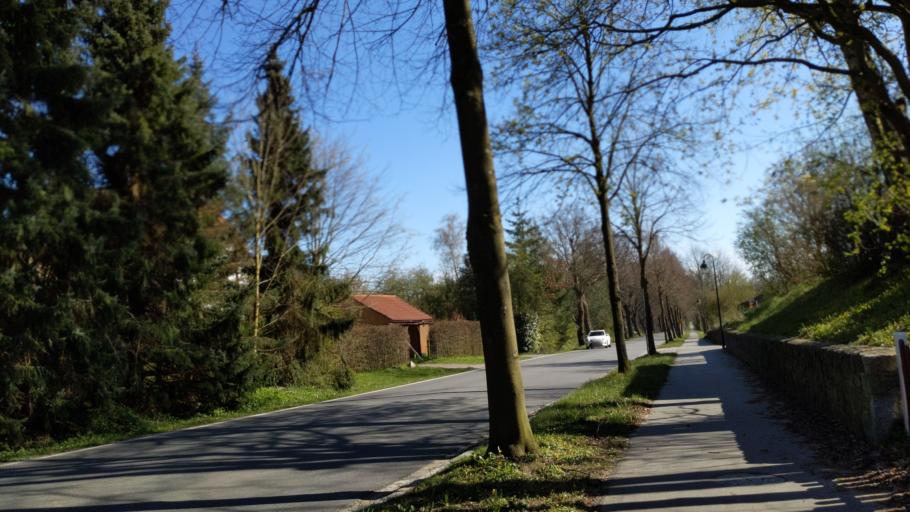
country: DE
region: Schleswig-Holstein
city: Eutin
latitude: 54.1044
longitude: 10.6121
